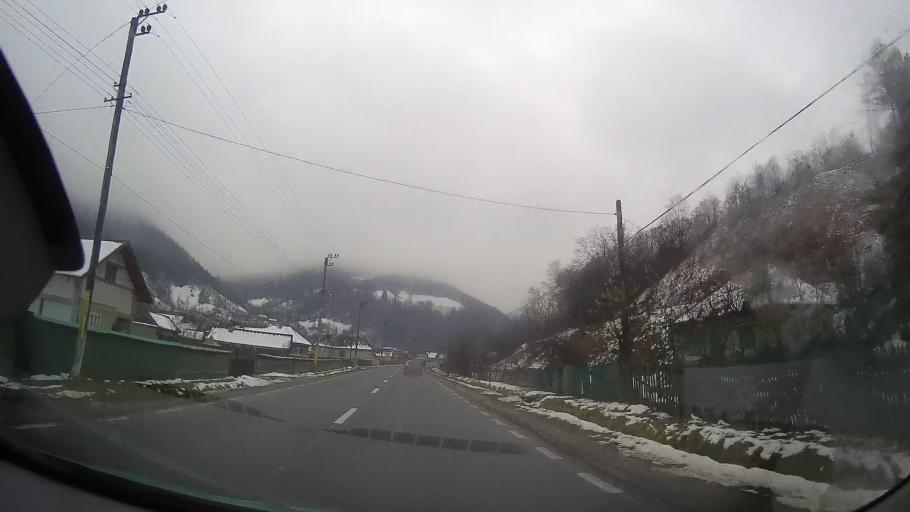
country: RO
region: Neamt
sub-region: Comuna Bicazu Ardelean
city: Bicazu Ardelean
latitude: 46.8564
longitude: 25.9360
